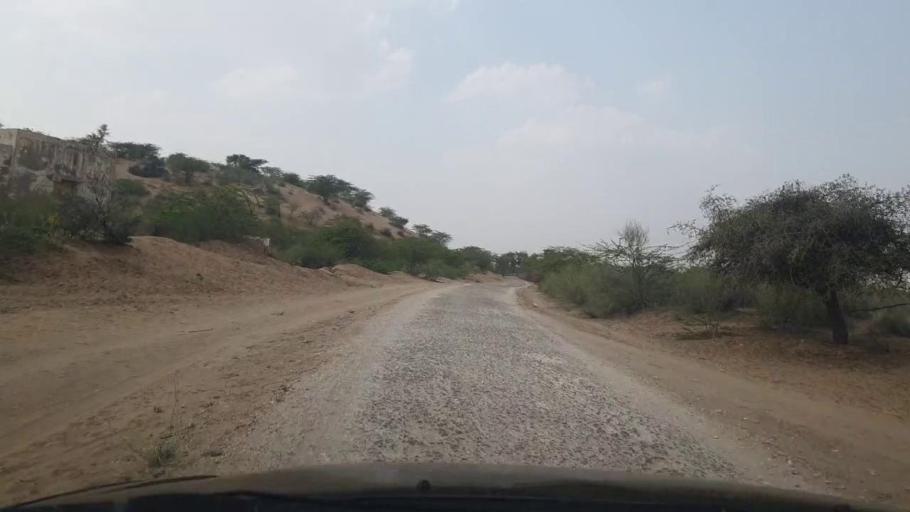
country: PK
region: Sindh
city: Islamkot
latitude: 24.9532
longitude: 70.6370
